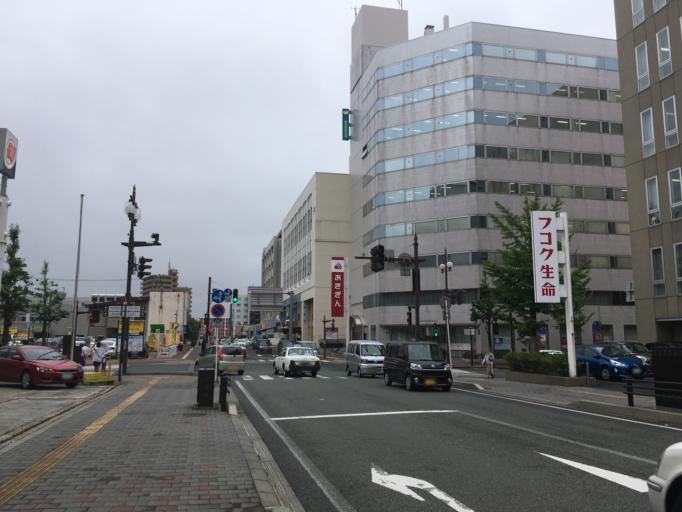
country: JP
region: Akita
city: Akita
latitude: 39.7163
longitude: 140.1254
